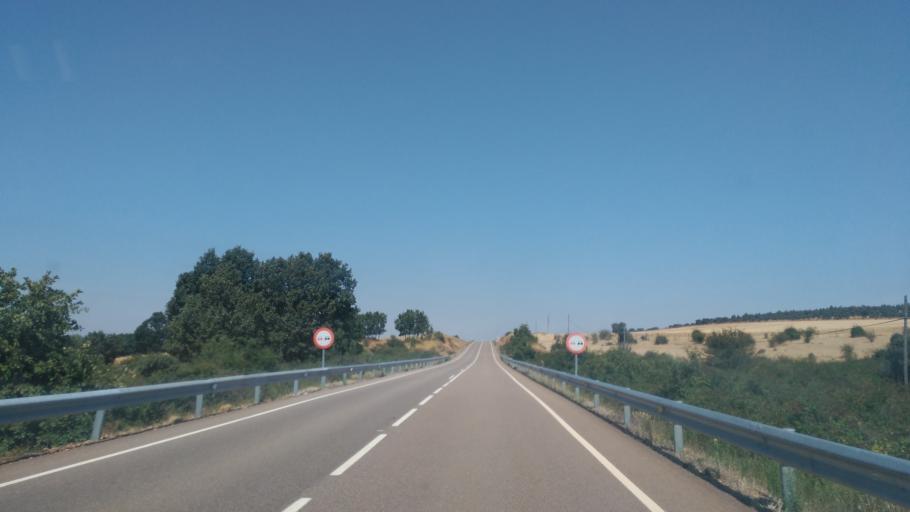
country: ES
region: Castille and Leon
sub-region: Provincia de Salamanca
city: Tamames
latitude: 40.6446
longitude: -6.1138
